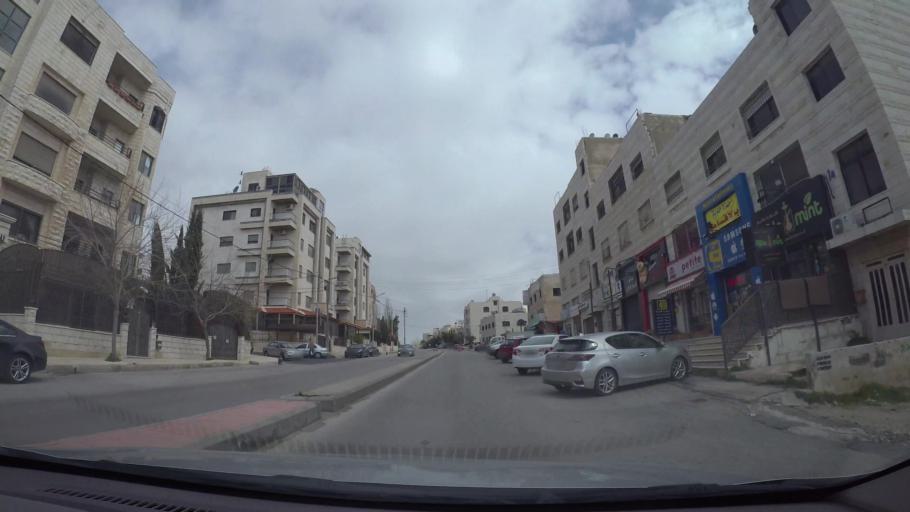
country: JO
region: Amman
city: Al Jubayhah
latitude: 32.0023
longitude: 35.8357
